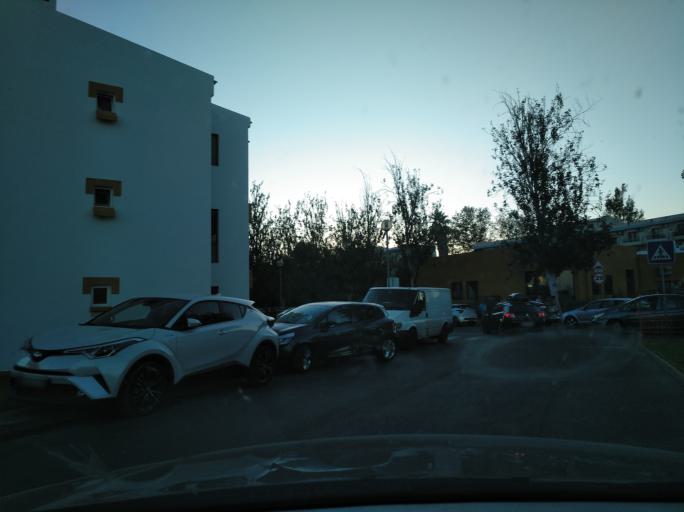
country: PT
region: Faro
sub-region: Tavira
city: Tavira
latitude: 37.1340
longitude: -7.6031
